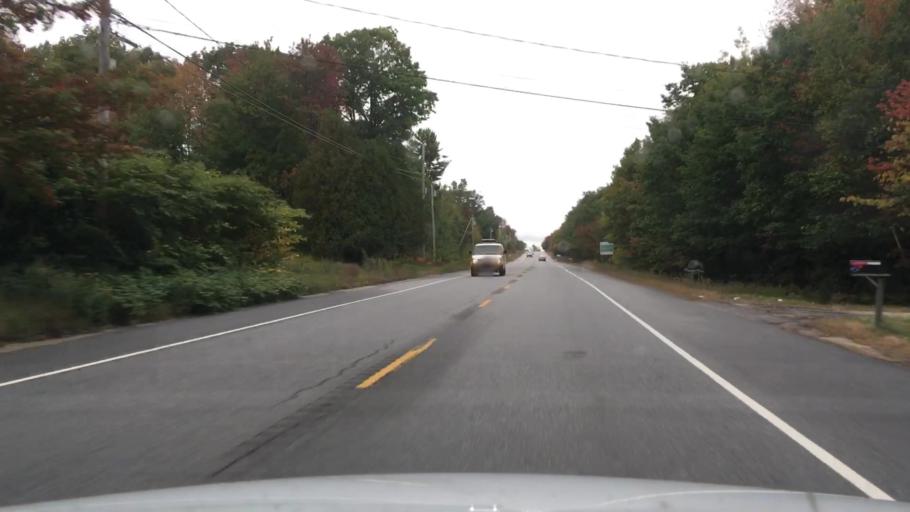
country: US
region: Maine
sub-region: Androscoggin County
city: Mechanic Falls
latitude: 44.1080
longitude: -70.4375
